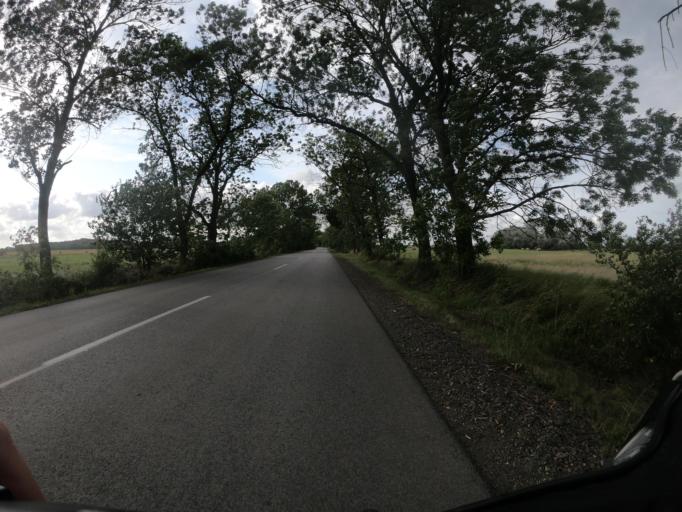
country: HU
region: Borsod-Abauj-Zemplen
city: Mezocsat
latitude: 47.8235
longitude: 20.8505
